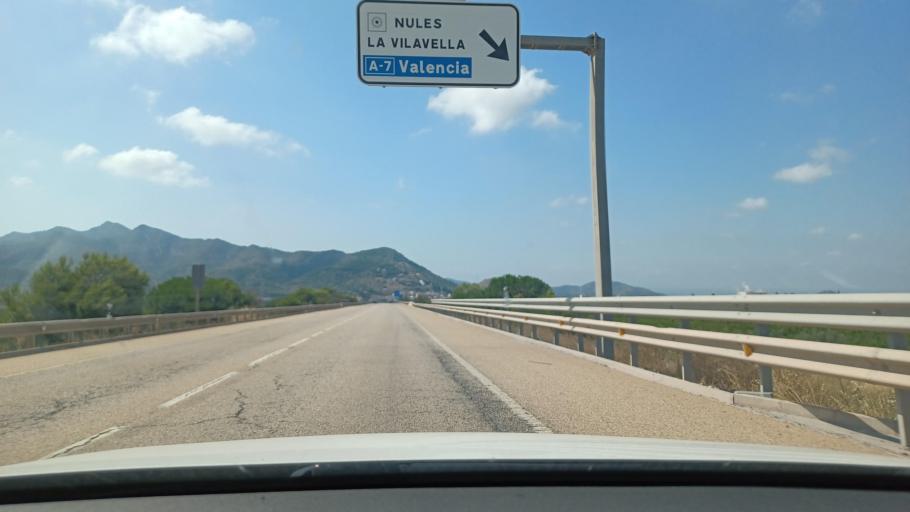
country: ES
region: Valencia
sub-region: Provincia de Castello
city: Villavieja
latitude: 39.8395
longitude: -0.1711
